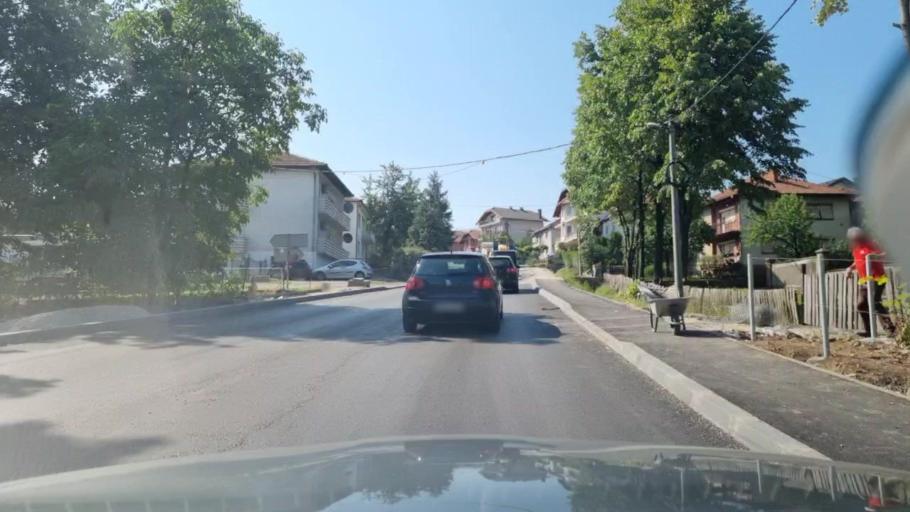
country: BA
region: Federation of Bosnia and Herzegovina
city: Gradacac
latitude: 44.8742
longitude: 18.4267
